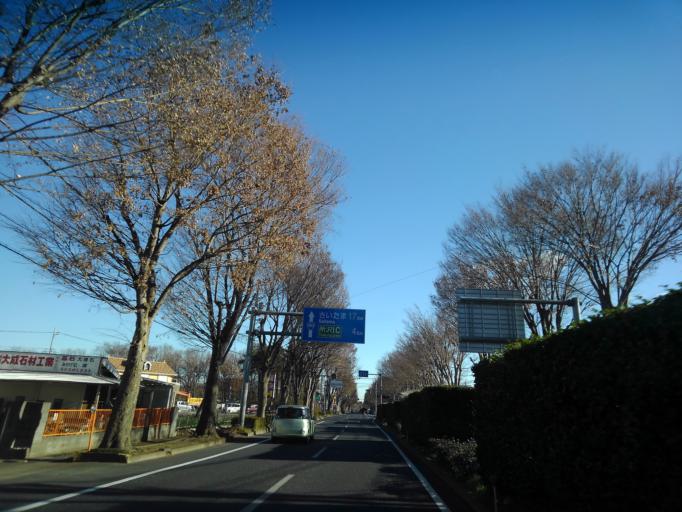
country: JP
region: Saitama
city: Tokorozawa
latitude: 35.8014
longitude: 139.5026
